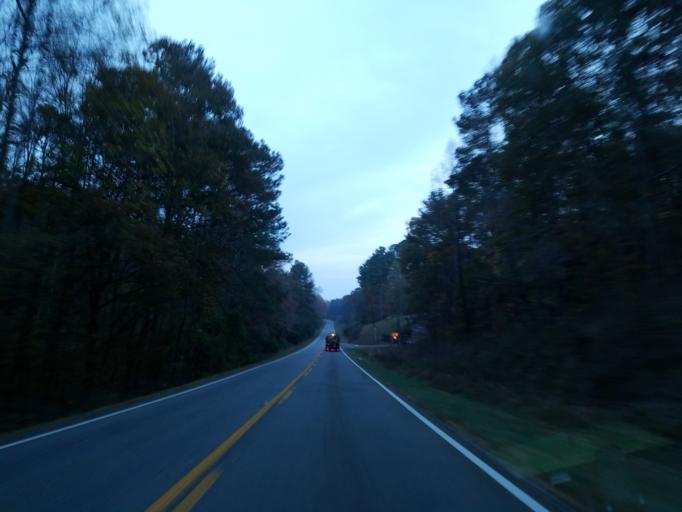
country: US
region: Georgia
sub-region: Pickens County
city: Jasper
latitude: 34.5202
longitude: -84.5694
